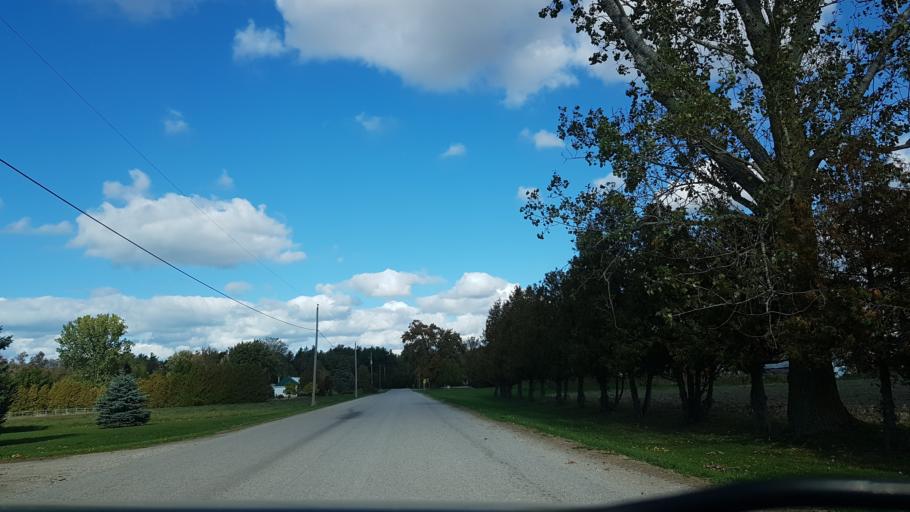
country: CA
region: Ontario
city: Lambton Shores
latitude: 43.2326
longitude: -81.7916
